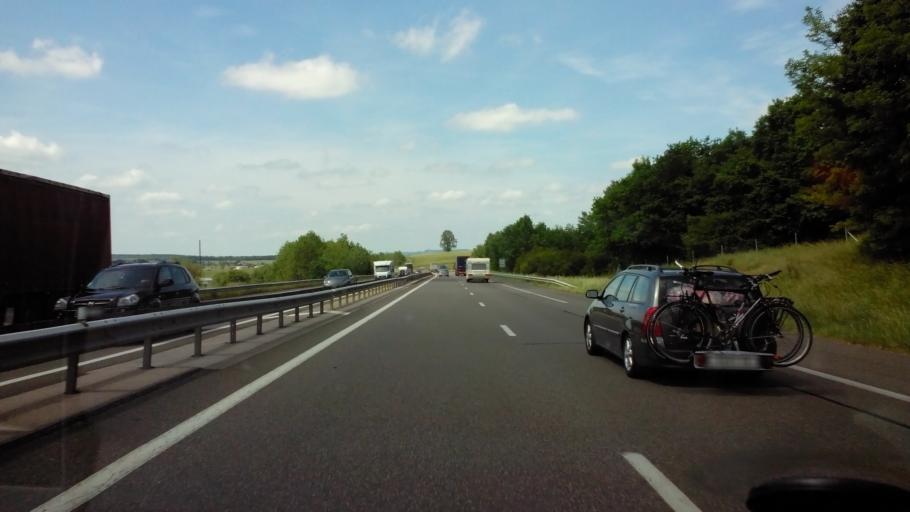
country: FR
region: Lorraine
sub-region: Departement des Vosges
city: Bulgneville
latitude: 48.2179
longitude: 5.8302
